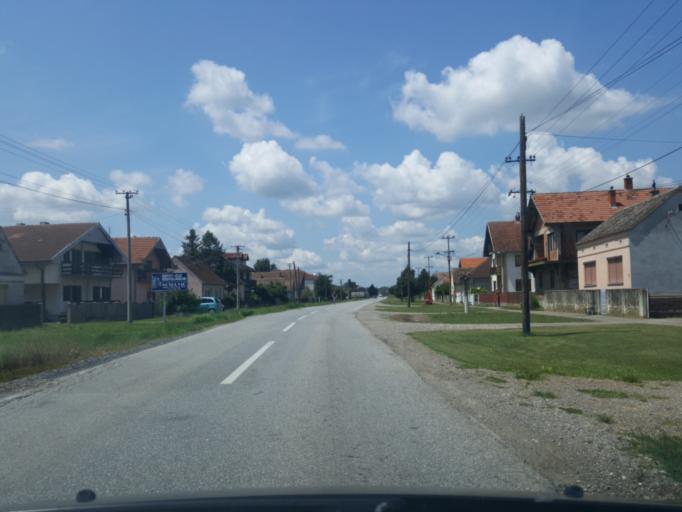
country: RS
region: Central Serbia
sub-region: Macvanski Okrug
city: Bogatic
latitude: 44.8406
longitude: 19.4906
